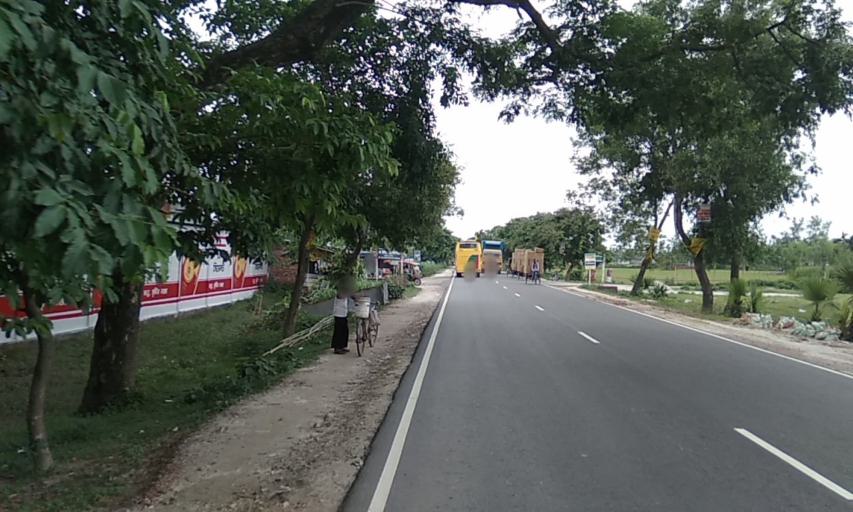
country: BD
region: Rangpur Division
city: Rangpur
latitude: 25.7972
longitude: 89.1951
